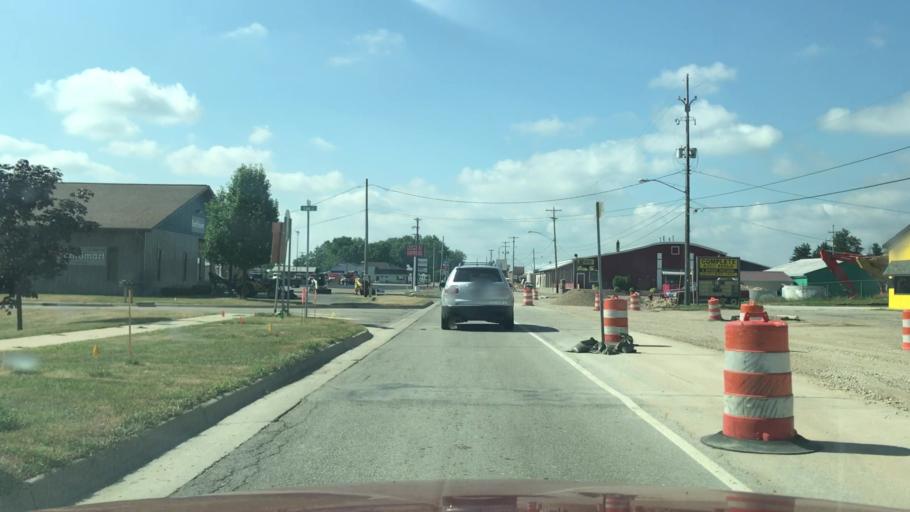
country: US
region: Michigan
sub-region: Newaygo County
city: Newaygo
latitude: 43.3315
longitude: -85.8105
